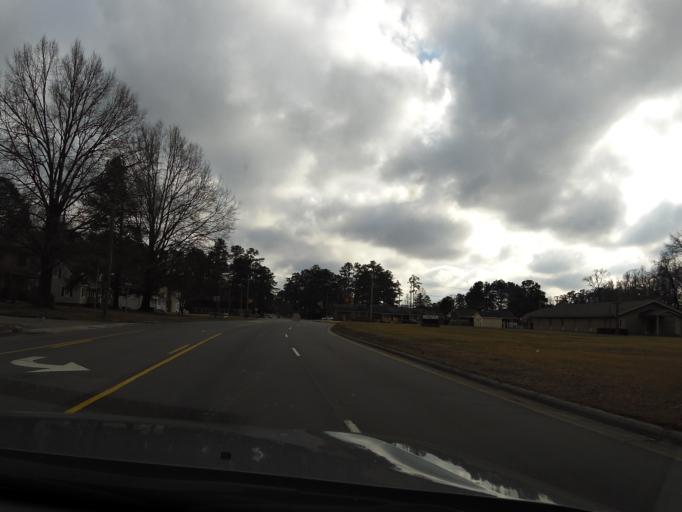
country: US
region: North Carolina
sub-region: Nash County
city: Rocky Mount
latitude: 35.9398
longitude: -77.8483
